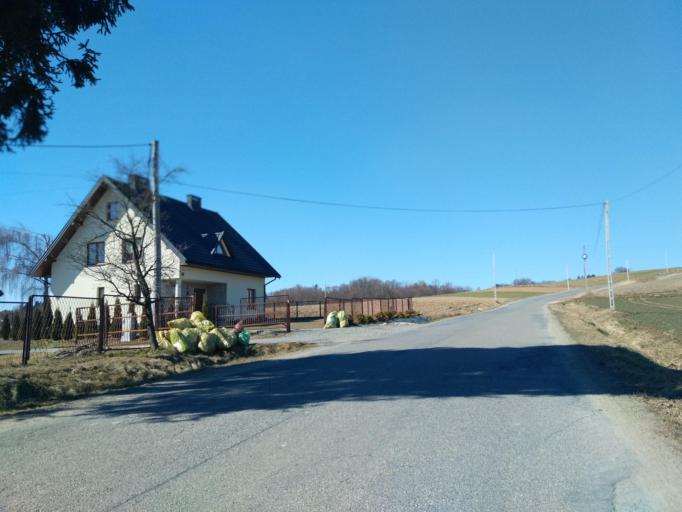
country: PL
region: Subcarpathian Voivodeship
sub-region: Powiat debicki
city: Brzostek
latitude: 49.9409
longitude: 21.4377
